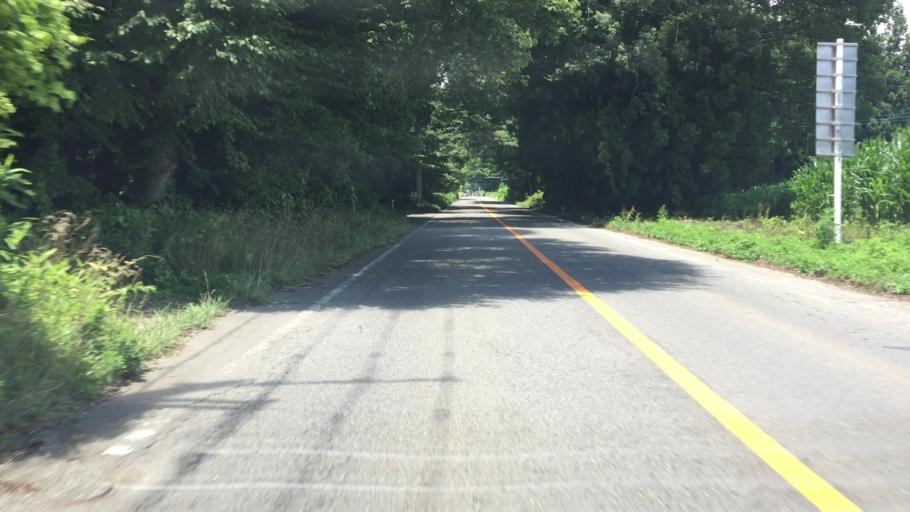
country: JP
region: Tochigi
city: Kuroiso
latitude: 37.0158
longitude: 139.9579
